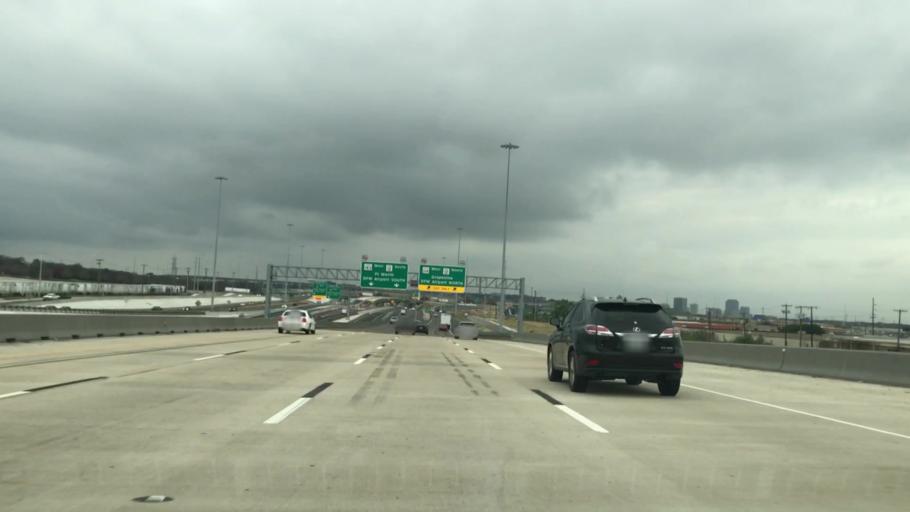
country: US
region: Texas
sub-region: Dallas County
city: Irving
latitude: 32.8338
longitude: -96.8955
